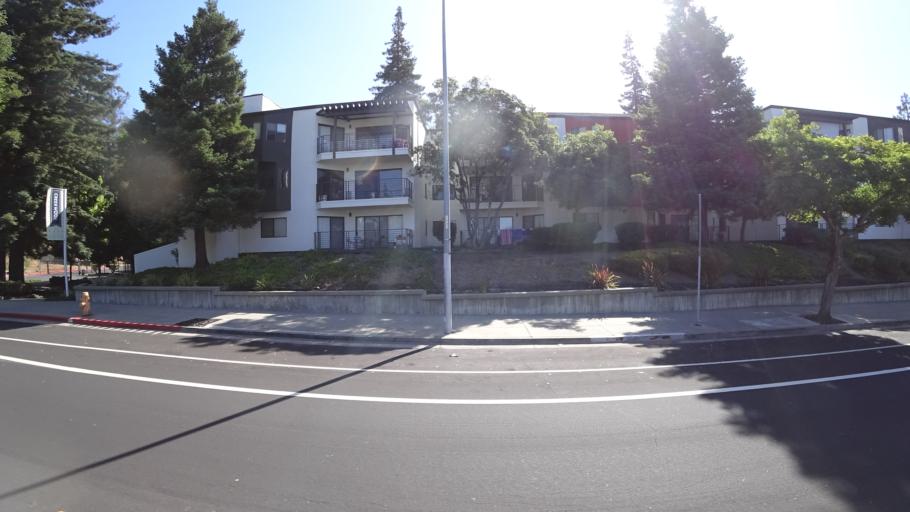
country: US
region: California
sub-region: Alameda County
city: Hayward
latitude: 37.6804
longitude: -122.0823
